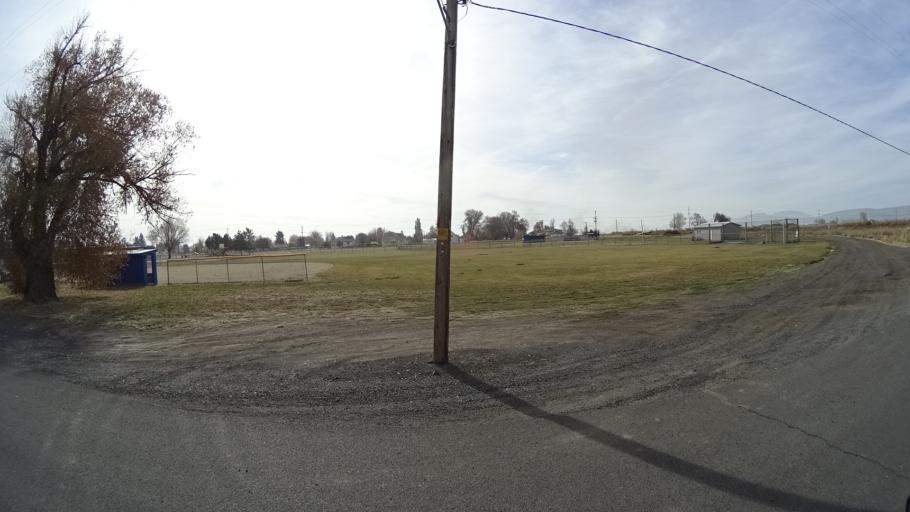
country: US
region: California
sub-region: Siskiyou County
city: Tulelake
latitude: 41.9560
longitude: -121.4803
